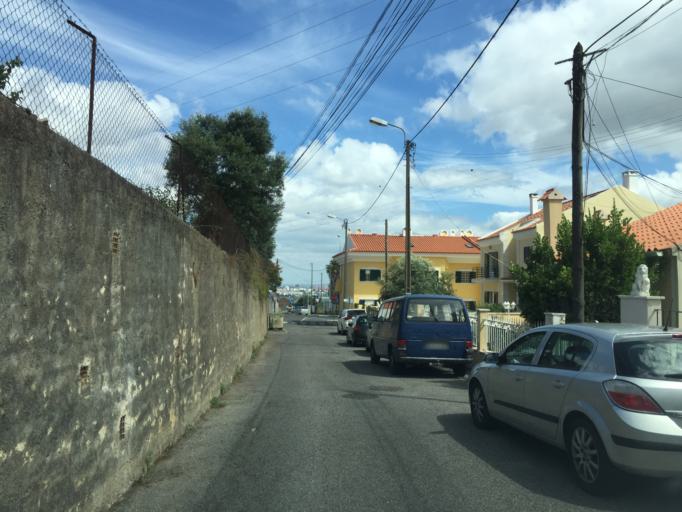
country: PT
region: Lisbon
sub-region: Odivelas
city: Famoes
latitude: 38.7888
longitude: -9.2277
